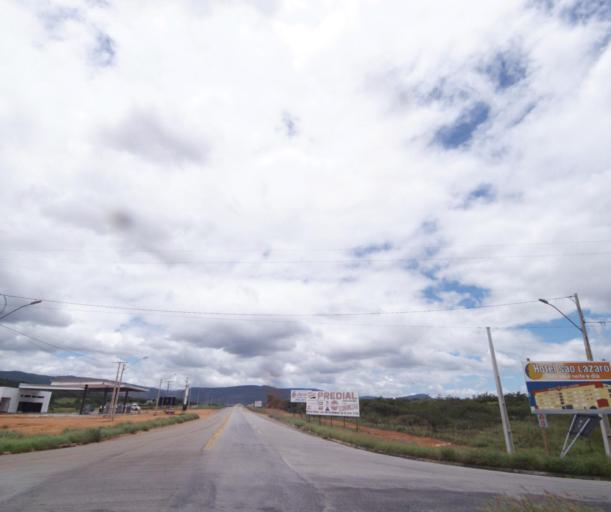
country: BR
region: Bahia
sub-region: Brumado
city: Brumado
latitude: -14.2147
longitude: -41.6461
